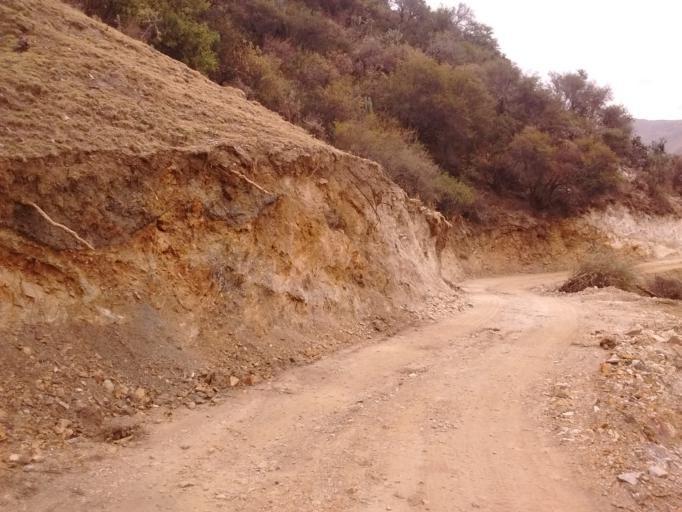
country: PE
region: Ayacucho
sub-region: Provincia de Victor Fajardo
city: Canaria
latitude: -13.8829
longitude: -73.9385
